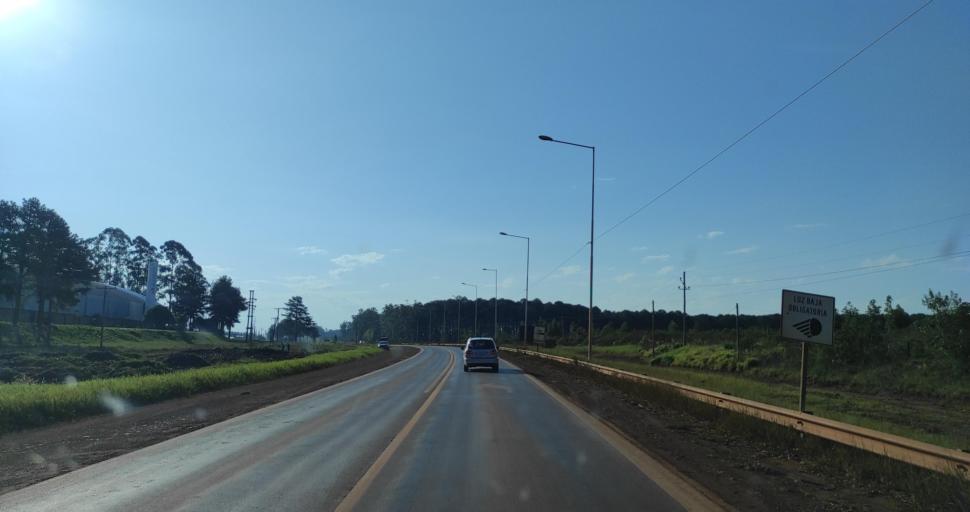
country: AR
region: Corrientes
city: Gobernador Ingeniero Valentin Virasoro
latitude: -28.0205
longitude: -56.0154
